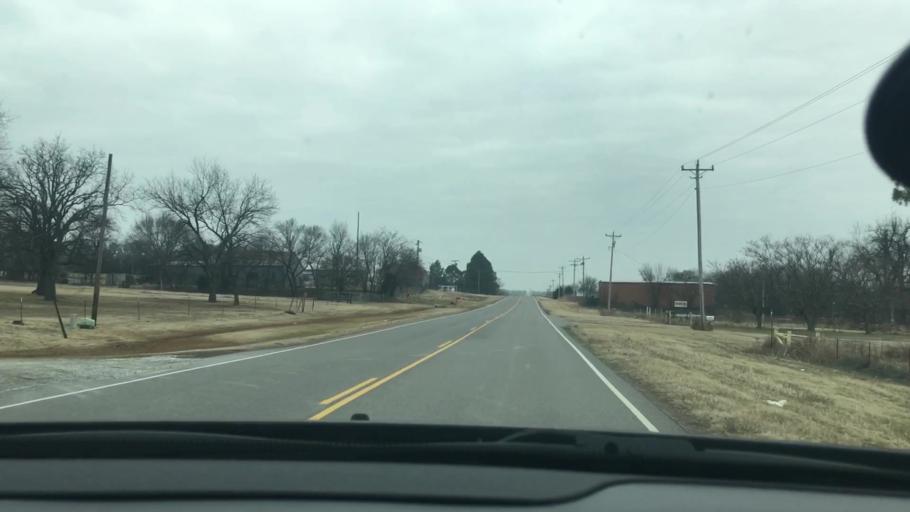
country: US
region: Oklahoma
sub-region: Carter County
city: Healdton
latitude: 34.2549
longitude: -97.4923
